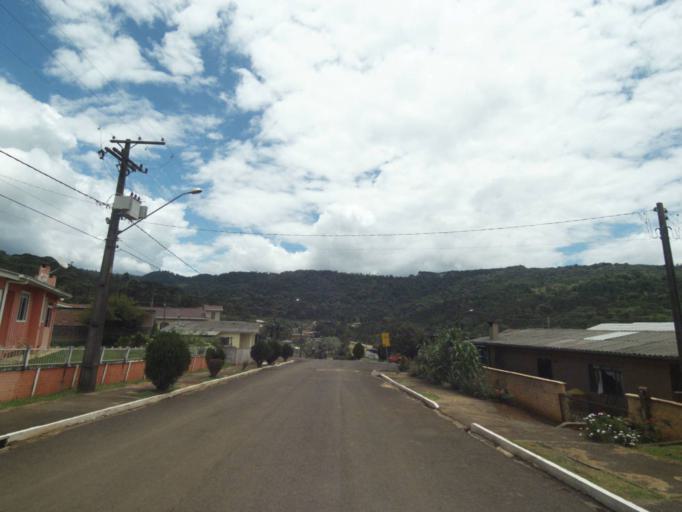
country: BR
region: Parana
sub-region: Pinhao
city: Pinhao
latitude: -26.1581
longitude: -51.5611
